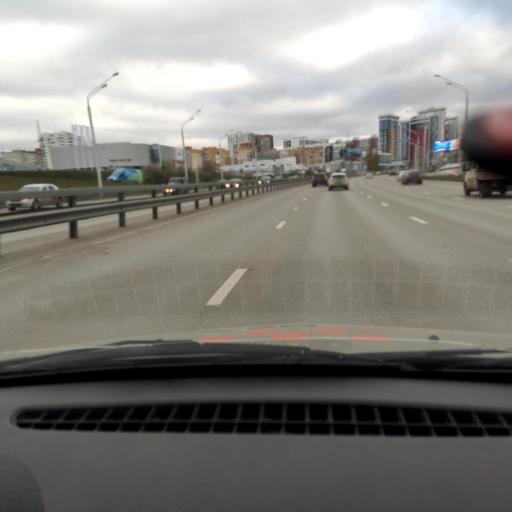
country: RU
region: Bashkortostan
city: Ufa
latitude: 54.7515
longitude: 56.0200
